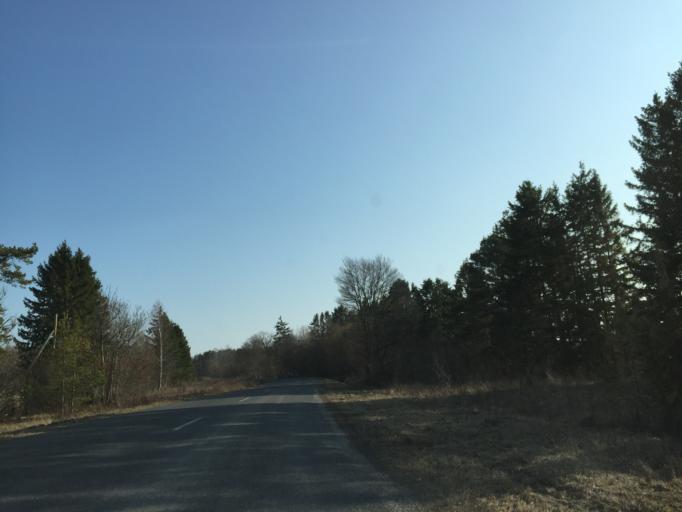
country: EE
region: Saare
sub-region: Orissaare vald
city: Orissaare
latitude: 58.6034
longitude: 23.3155
